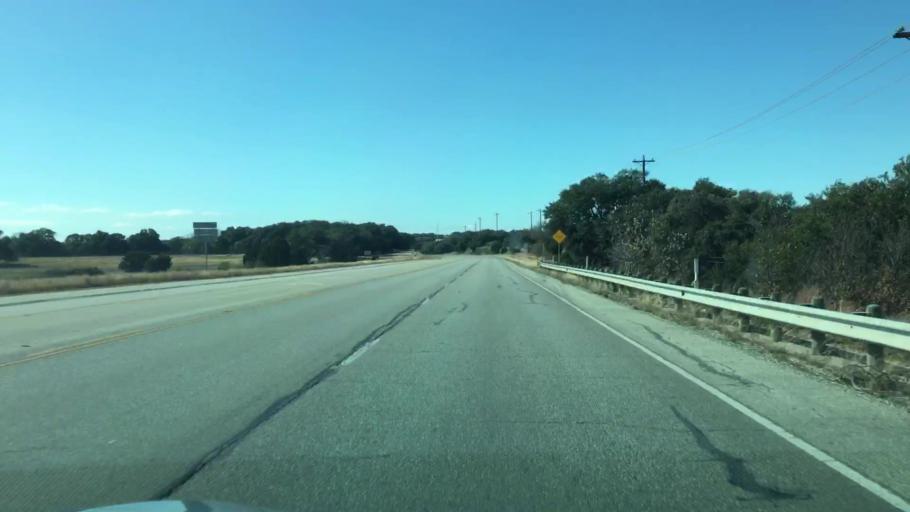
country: US
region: Texas
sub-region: Hays County
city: Dripping Springs
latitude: 30.2068
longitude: -98.1430
